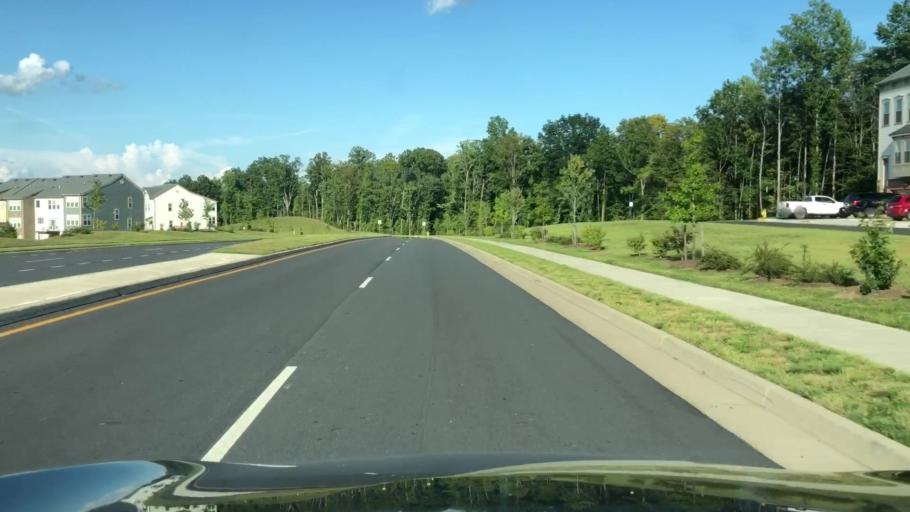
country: US
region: Virginia
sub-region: Stafford County
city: Stafford
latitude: 38.4280
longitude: -77.4640
